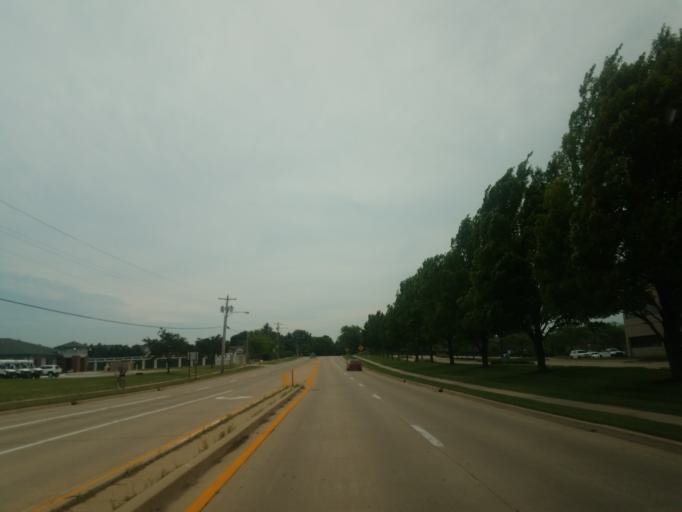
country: US
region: Illinois
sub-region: McLean County
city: Normal
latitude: 40.5019
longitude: -88.9388
